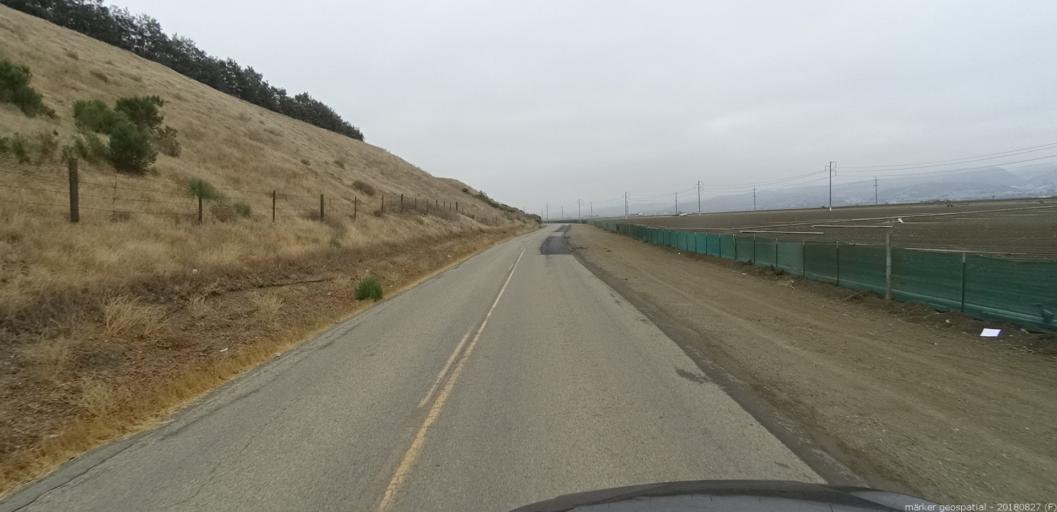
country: US
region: California
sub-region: Monterey County
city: King City
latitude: 36.2492
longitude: -121.1360
